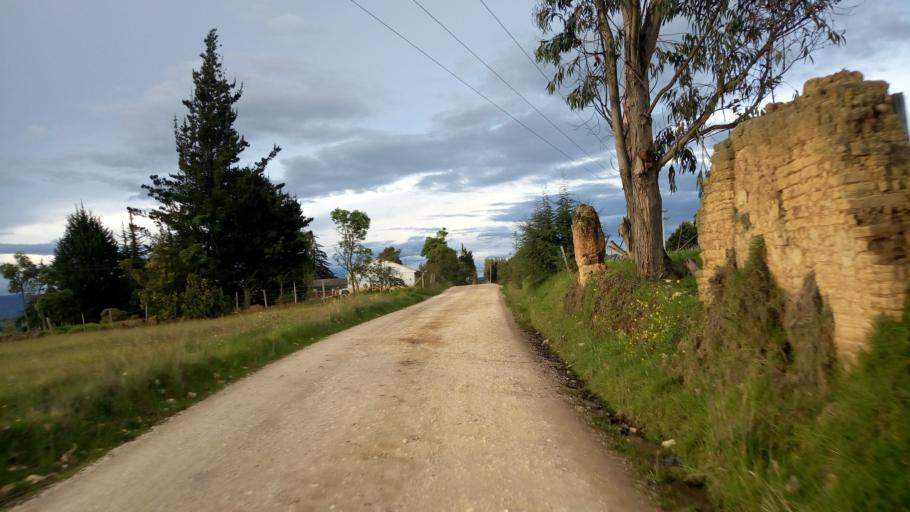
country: CO
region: Boyaca
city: Toca
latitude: 5.5844
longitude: -73.1714
